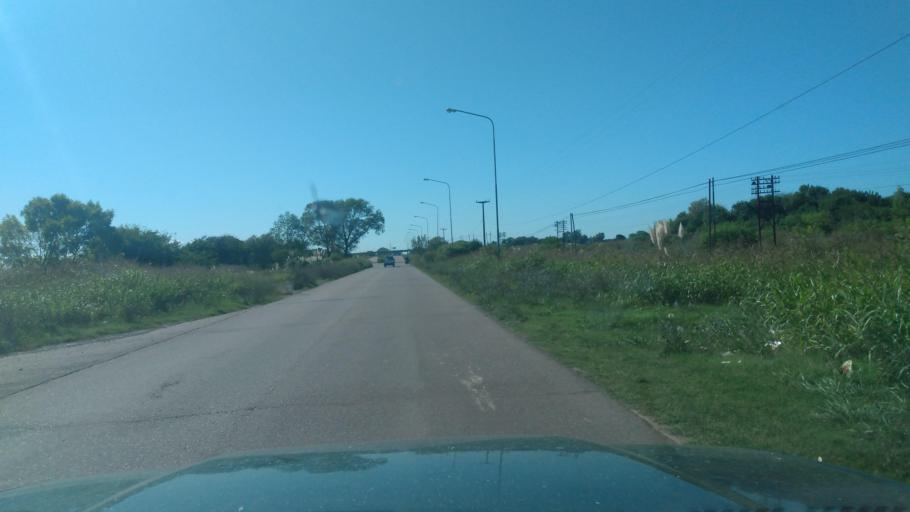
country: AR
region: Buenos Aires
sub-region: Partido de Lujan
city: Lujan
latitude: -34.5864
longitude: -59.0479
